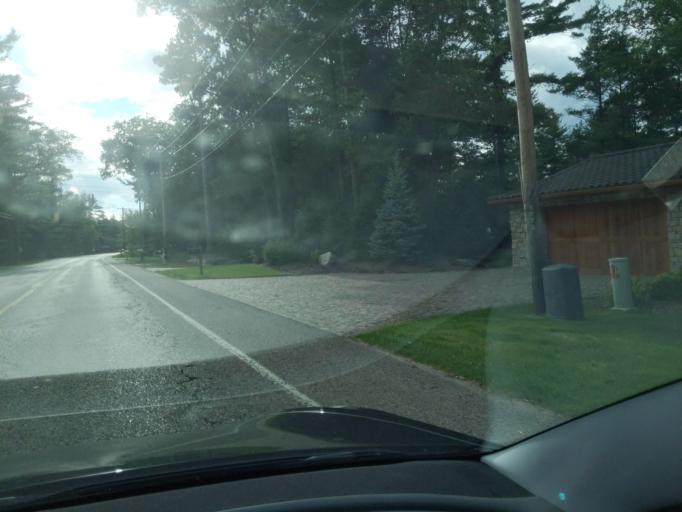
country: US
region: Michigan
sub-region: Kalkaska County
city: Rapid City
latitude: 44.8545
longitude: -85.3066
